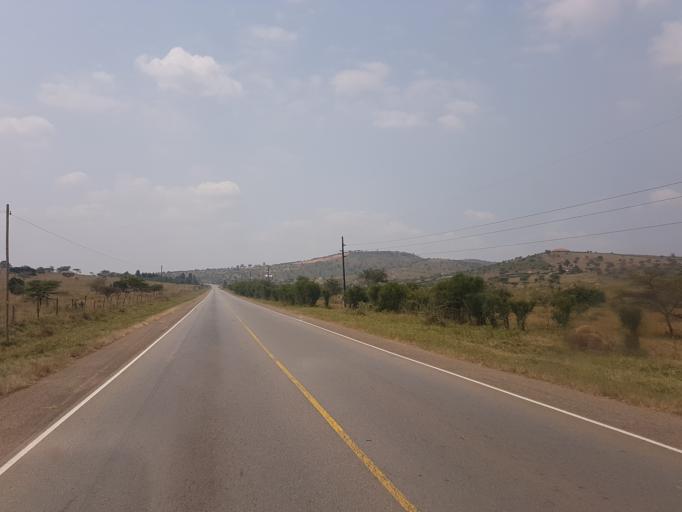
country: UG
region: Western Region
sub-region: Mbarara District
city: Mbarara
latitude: -0.5068
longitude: 30.8433
